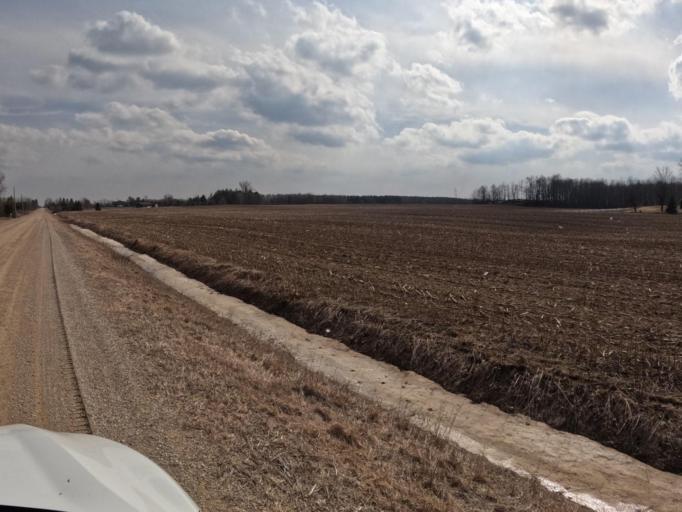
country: CA
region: Ontario
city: Shelburne
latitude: 43.9490
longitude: -80.3128
